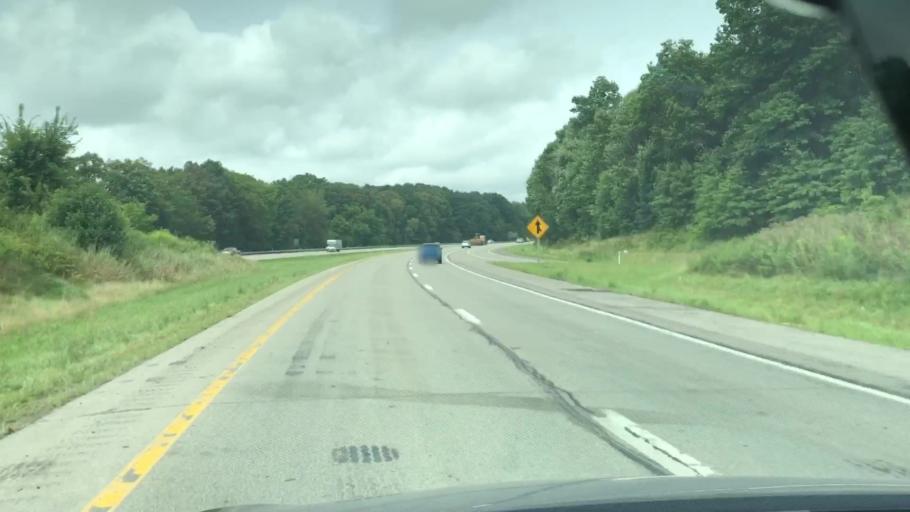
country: US
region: Pennsylvania
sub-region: Butler County
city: Slippery Rock
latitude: 41.0391
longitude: -80.1260
